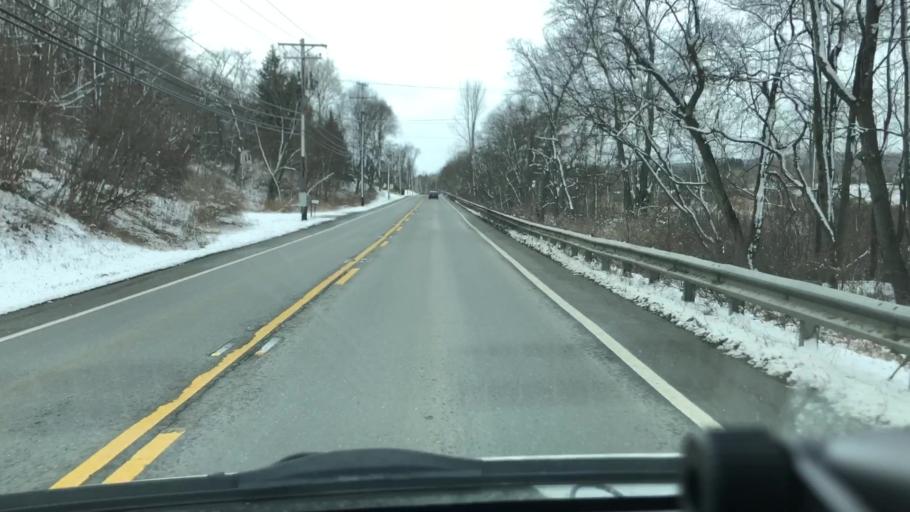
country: US
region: Massachusetts
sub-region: Franklin County
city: Greenfield
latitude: 42.5584
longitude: -72.5969
